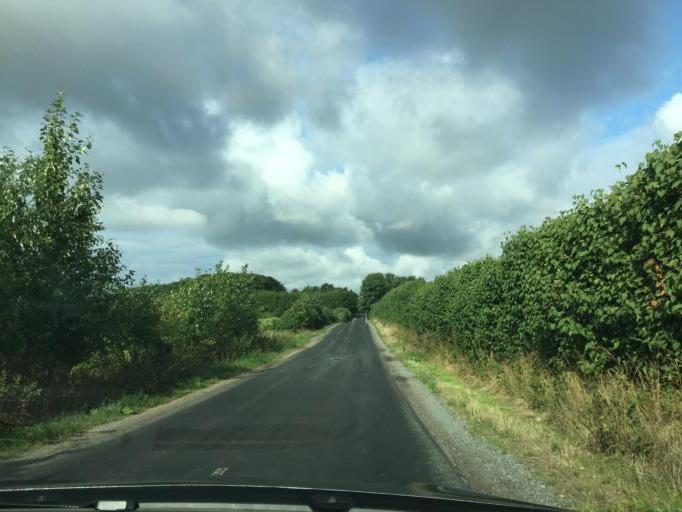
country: DK
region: South Denmark
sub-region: Faaborg-Midtfyn Kommune
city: Faaborg
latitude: 55.1930
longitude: 10.2262
